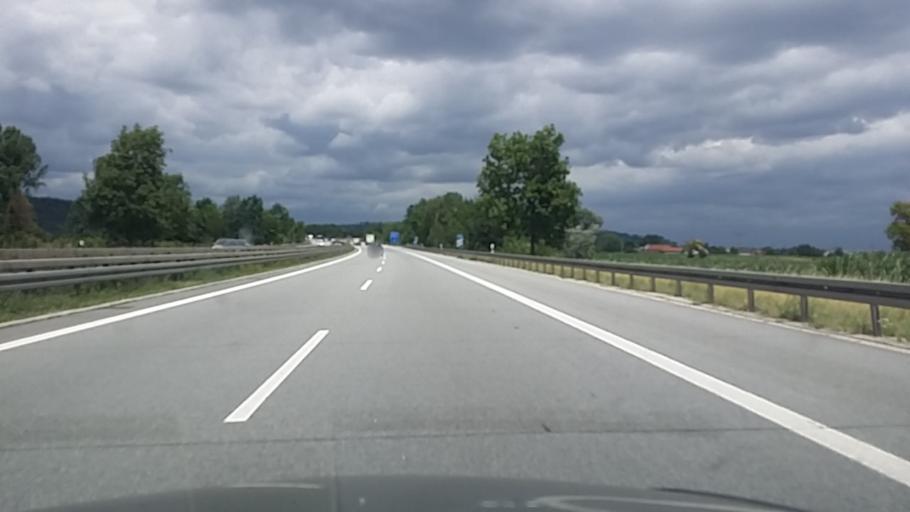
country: DE
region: Bavaria
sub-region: Lower Bavaria
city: Eching
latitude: 48.5272
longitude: 12.0697
